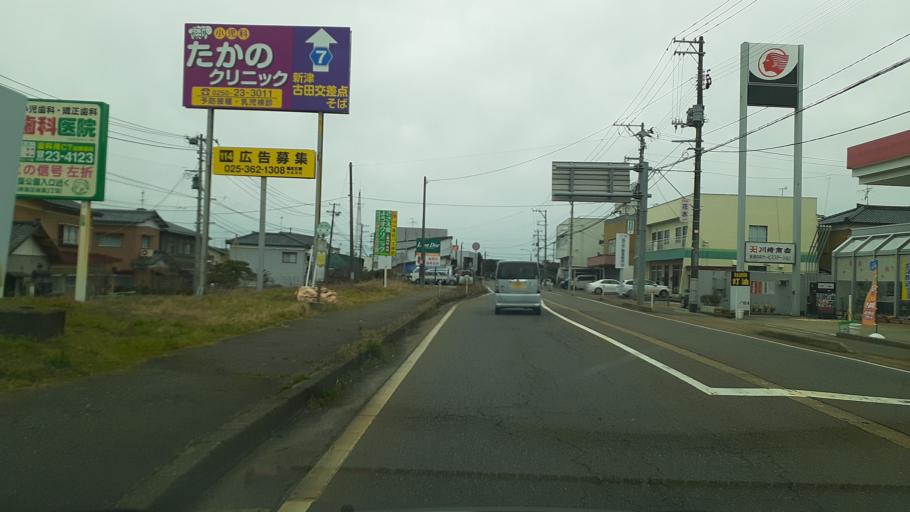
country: JP
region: Niigata
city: Niitsu-honcho
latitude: 37.7939
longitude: 139.1313
